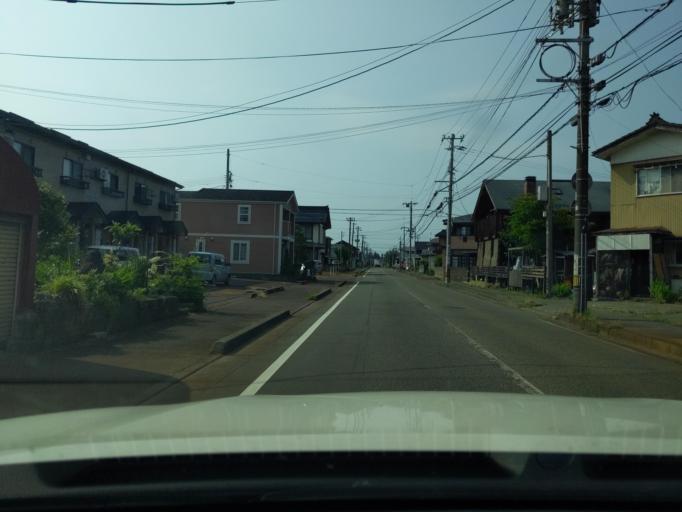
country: JP
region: Niigata
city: Nagaoka
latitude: 37.4303
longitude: 138.8602
